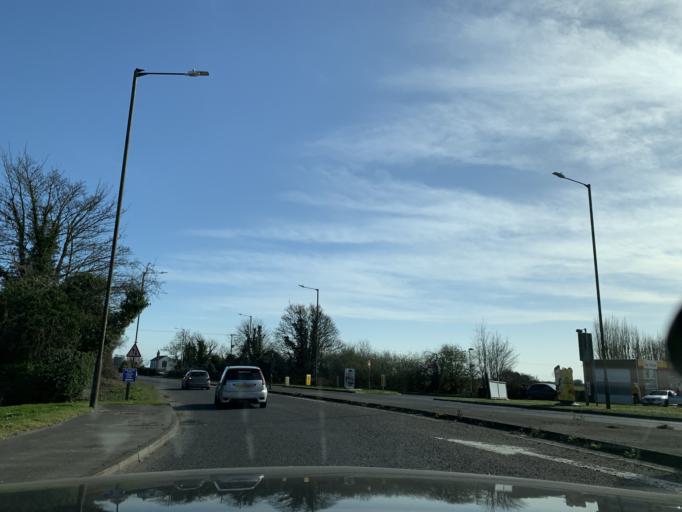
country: GB
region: England
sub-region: Kent
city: Romney Marsh
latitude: 51.0071
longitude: 0.8584
